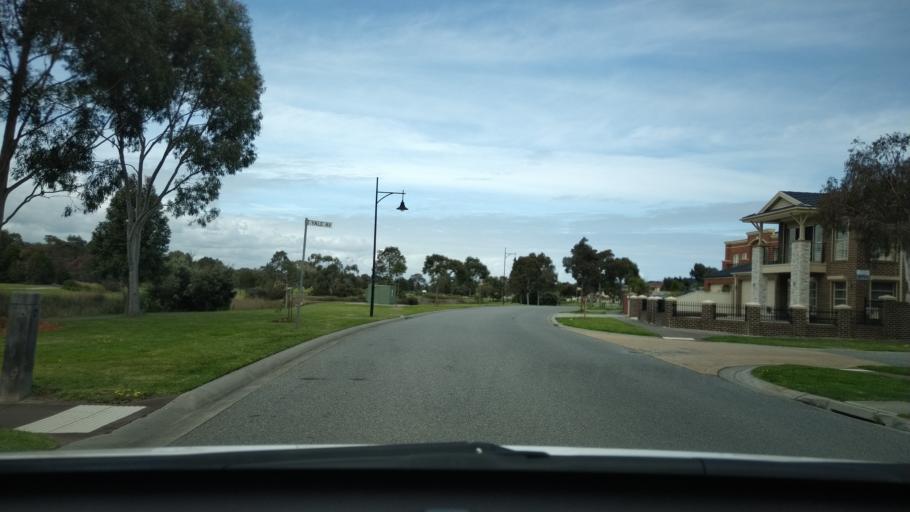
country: AU
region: Victoria
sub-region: Greater Dandenong
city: Keysborough
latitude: -37.9993
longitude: 145.1517
